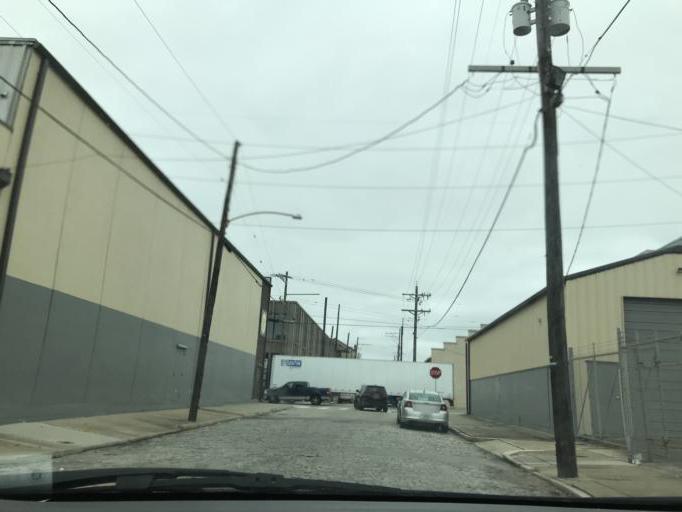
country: US
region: Louisiana
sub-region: Jefferson Parish
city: Gretna
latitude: 29.9281
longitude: -90.0676
